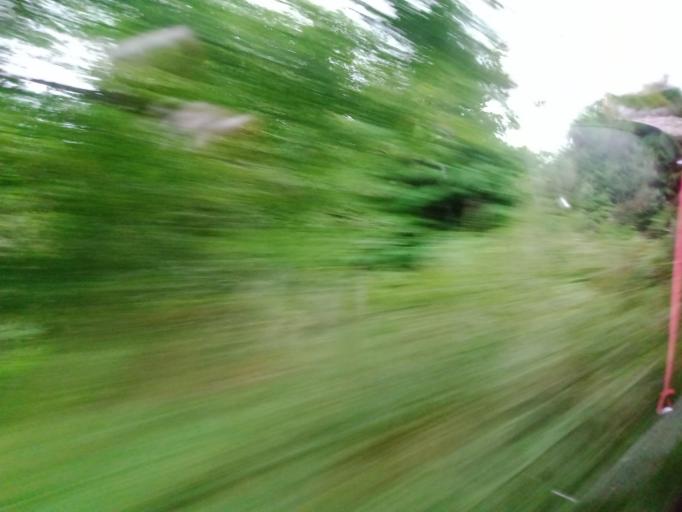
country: IE
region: Munster
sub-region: Waterford
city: Dungarvan
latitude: 52.0473
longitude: -7.6543
